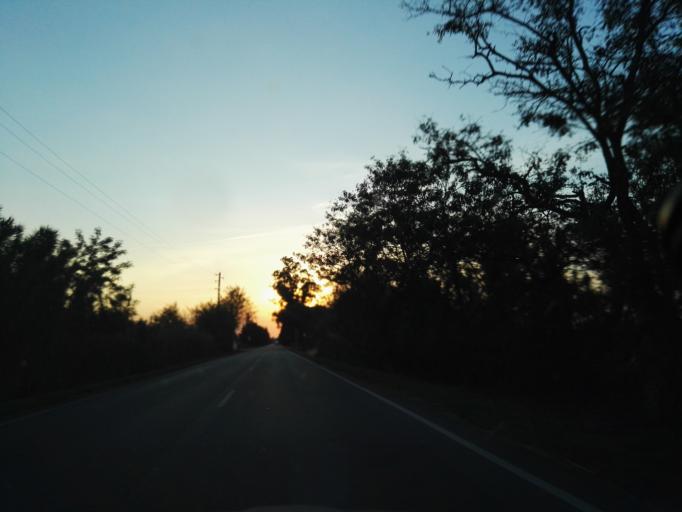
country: PT
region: Santarem
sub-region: Coruche
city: Coruche
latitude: 38.9707
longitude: -8.4677
